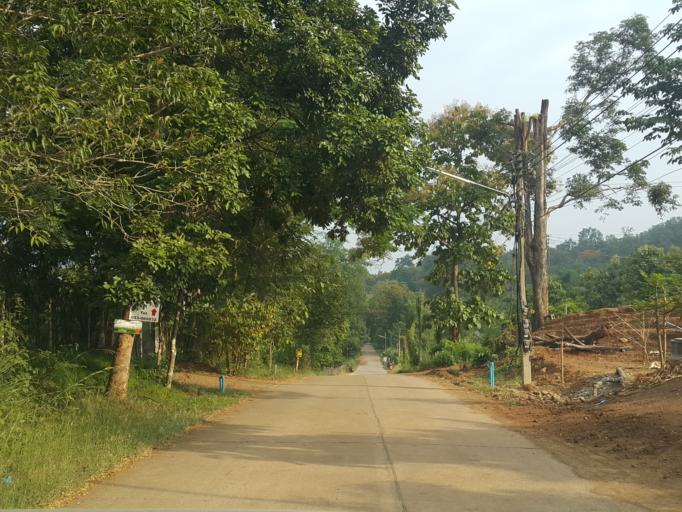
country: TH
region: Chiang Mai
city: Pai
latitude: 19.3650
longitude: 98.4497
